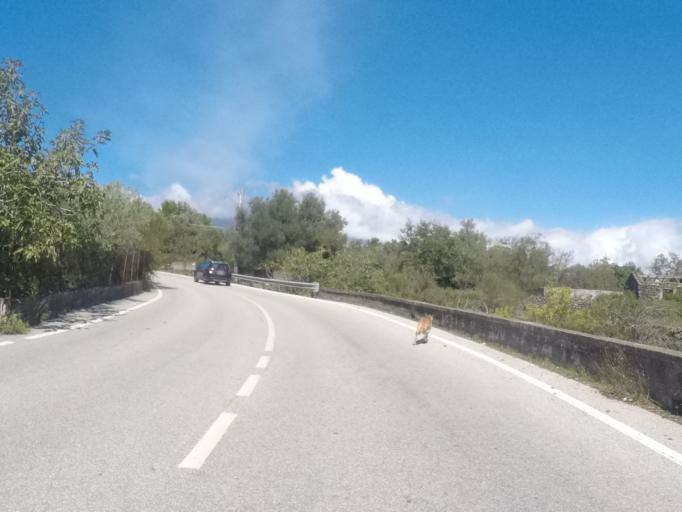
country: IT
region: Sicily
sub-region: Catania
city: Nicolosi
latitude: 37.6321
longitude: 14.9886
